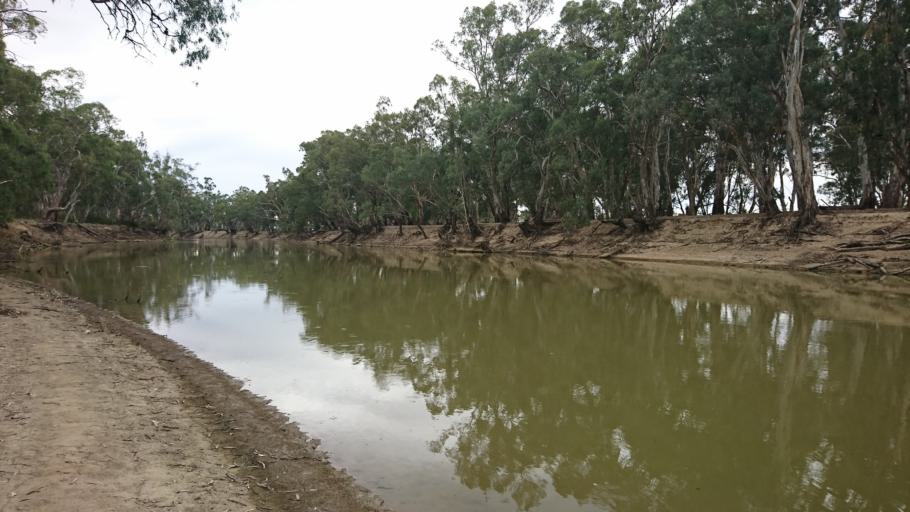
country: AU
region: Victoria
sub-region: Swan Hill
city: Swan Hill
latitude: -35.1250
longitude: 143.3748
